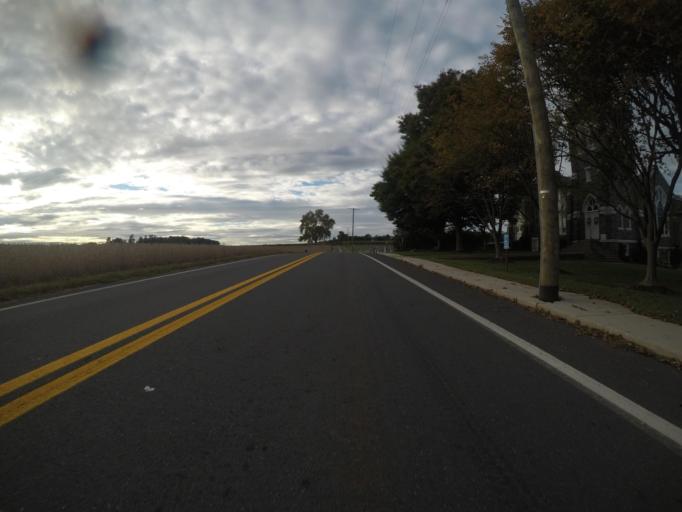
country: US
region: Maryland
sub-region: Carroll County
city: Hampstead
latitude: 39.5550
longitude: -76.8809
